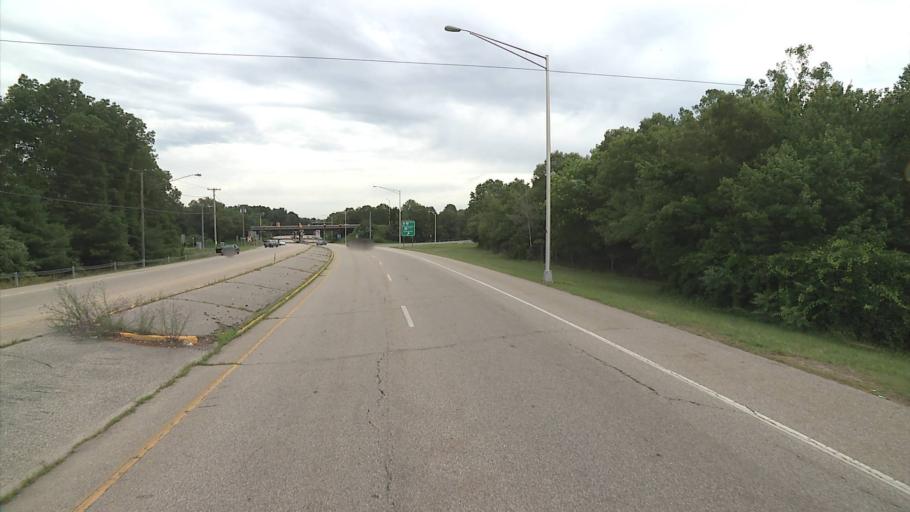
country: US
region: Connecticut
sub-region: New London County
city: Poquonock Bridge
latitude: 41.3596
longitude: -72.0279
